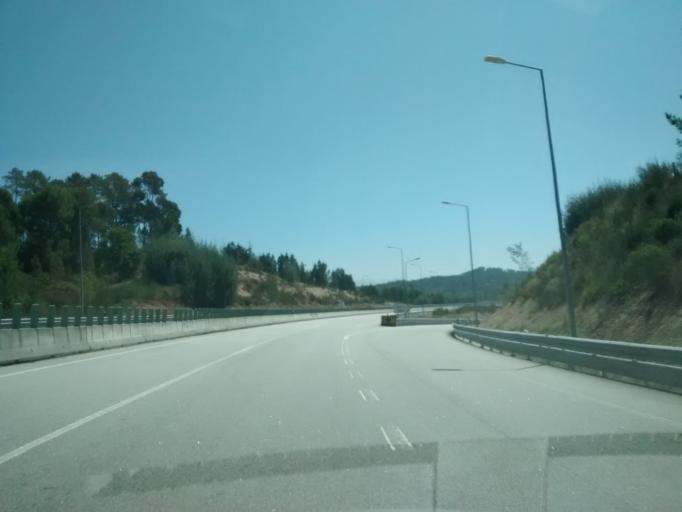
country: PT
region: Coimbra
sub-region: Tabua
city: Tabua
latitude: 40.3683
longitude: -8.0073
